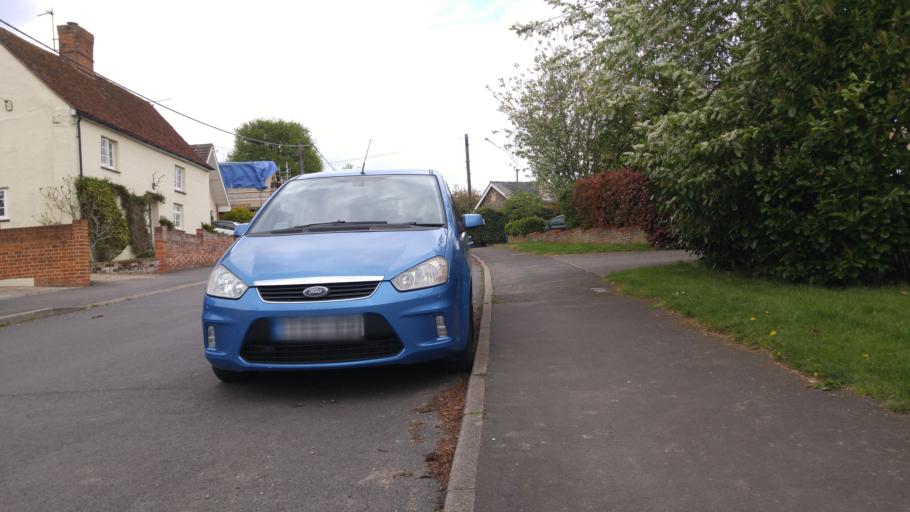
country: GB
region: England
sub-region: Essex
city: Earls Colne
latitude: 51.9409
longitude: 0.6885
